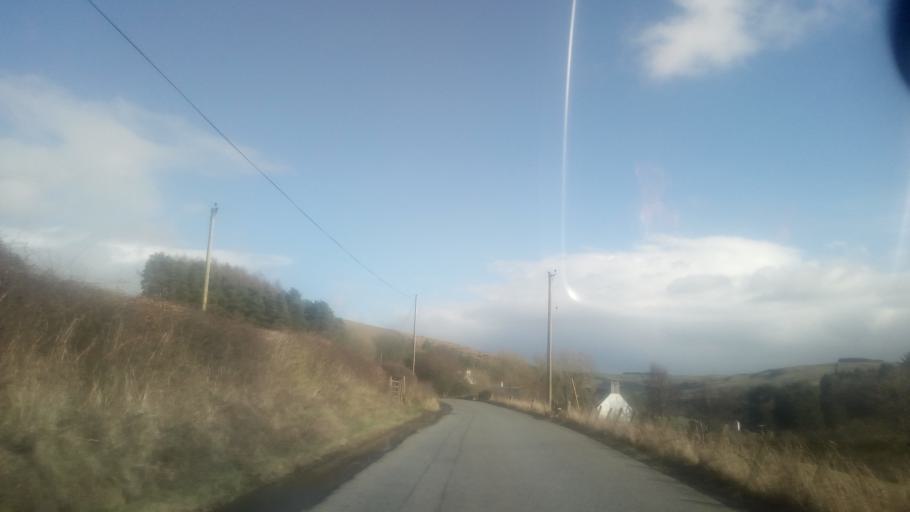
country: GB
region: Scotland
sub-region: The Scottish Borders
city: Hawick
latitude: 55.4177
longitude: -2.8626
